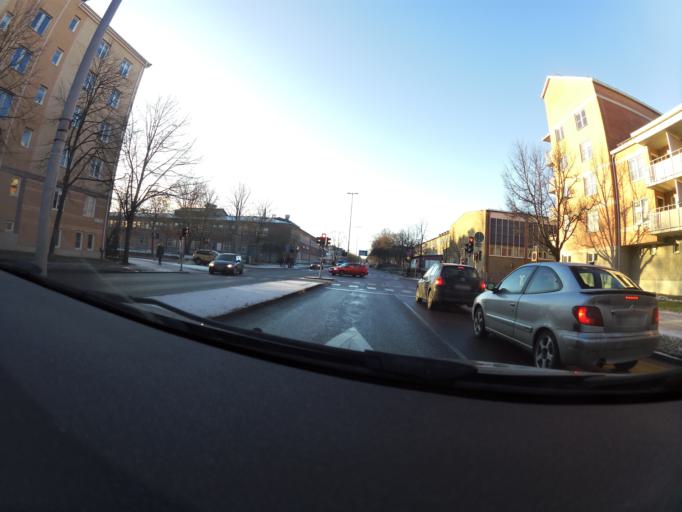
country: SE
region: Gaevleborg
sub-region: Gavle Kommun
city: Gavle
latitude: 60.6684
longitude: 17.1554
